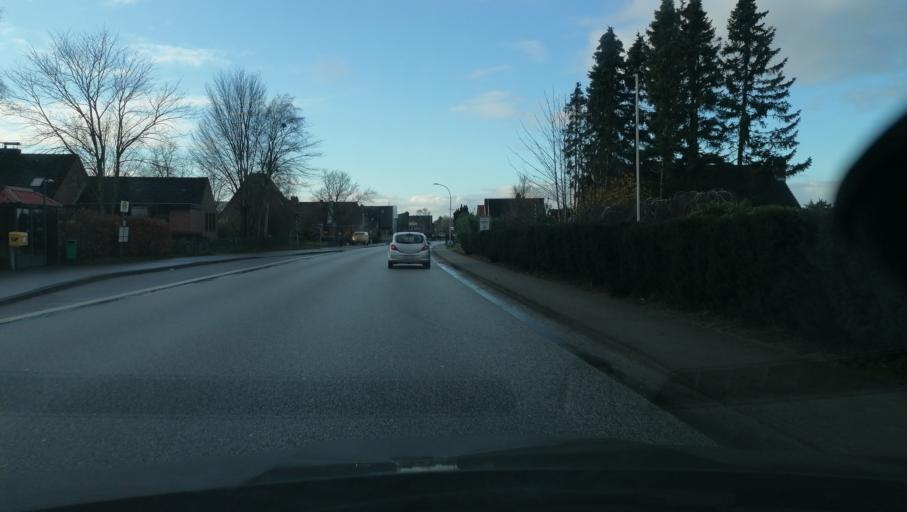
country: DE
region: Schleswig-Holstein
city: Nindorf
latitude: 54.0878
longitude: 9.1019
